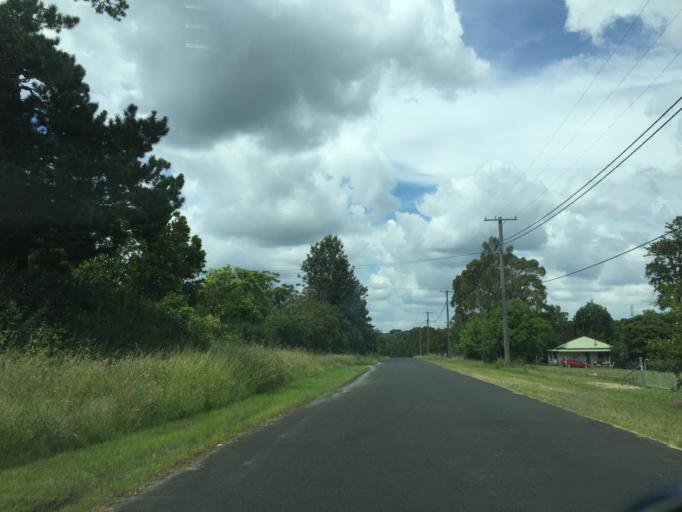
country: AU
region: New South Wales
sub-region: Hornsby Shire
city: Galston
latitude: -33.6552
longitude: 151.0467
